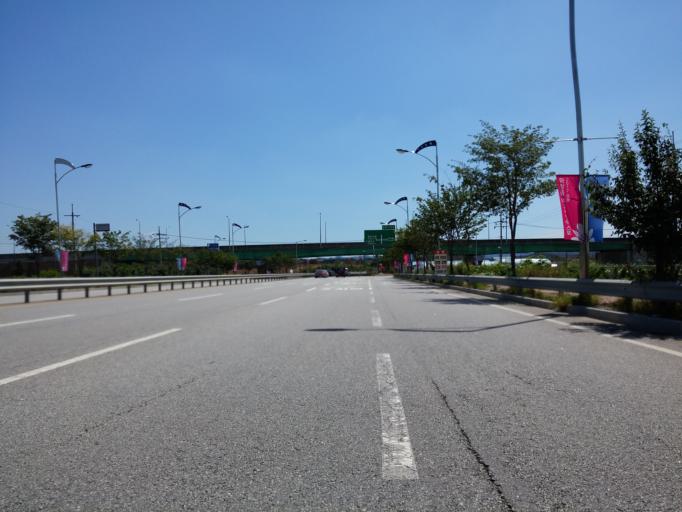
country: KR
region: Chungcheongbuk-do
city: Cheongju-si
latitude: 36.6206
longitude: 127.3405
